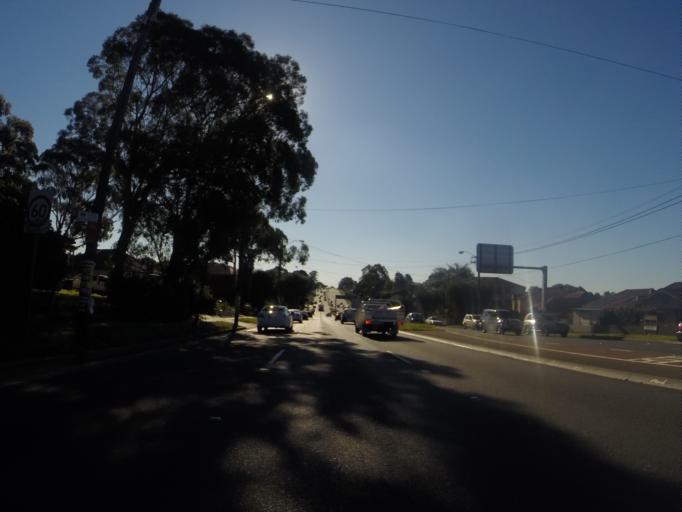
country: AU
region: New South Wales
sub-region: Canterbury
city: Roselands
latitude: -33.9389
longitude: 151.0752
